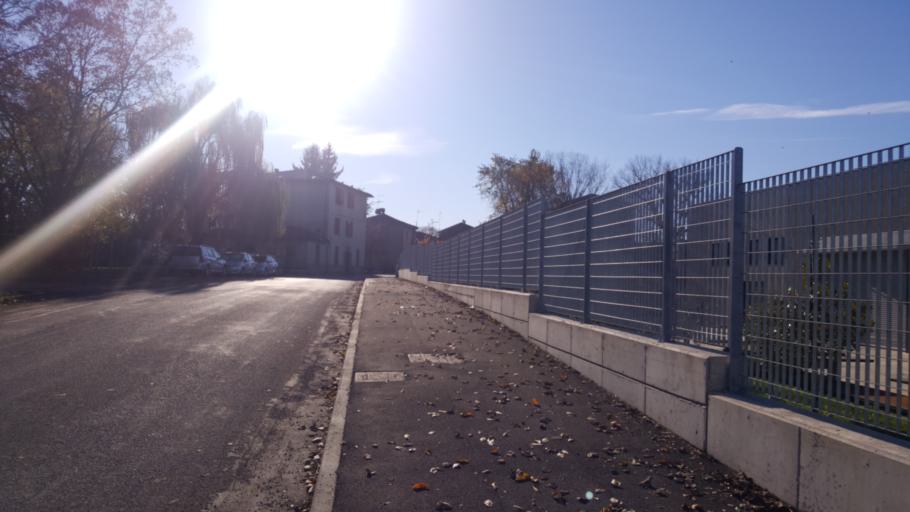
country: IT
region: Emilia-Romagna
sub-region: Provincia di Piacenza
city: Fiorenzuola d'Arda
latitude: 44.9329
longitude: 9.9080
